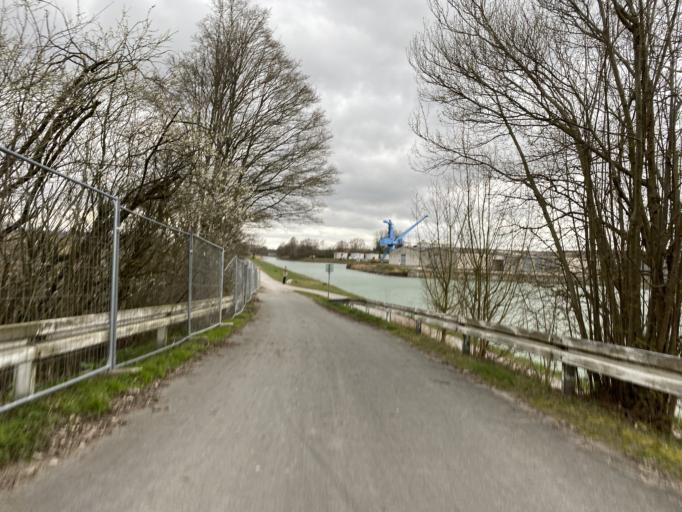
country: DE
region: North Rhine-Westphalia
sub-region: Regierungsbezirk Arnsberg
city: Welver
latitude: 51.6843
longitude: 7.9438
